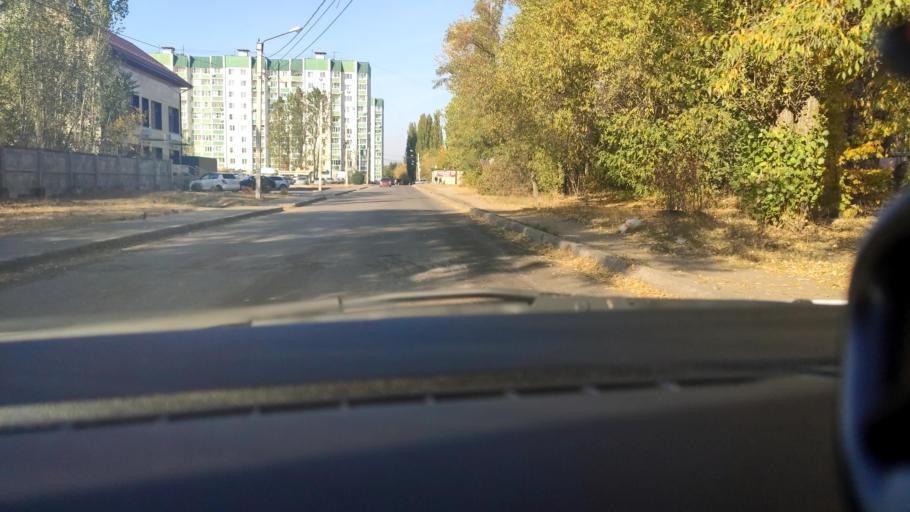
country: RU
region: Voronezj
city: Pridonskoy
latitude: 51.6242
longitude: 39.0686
